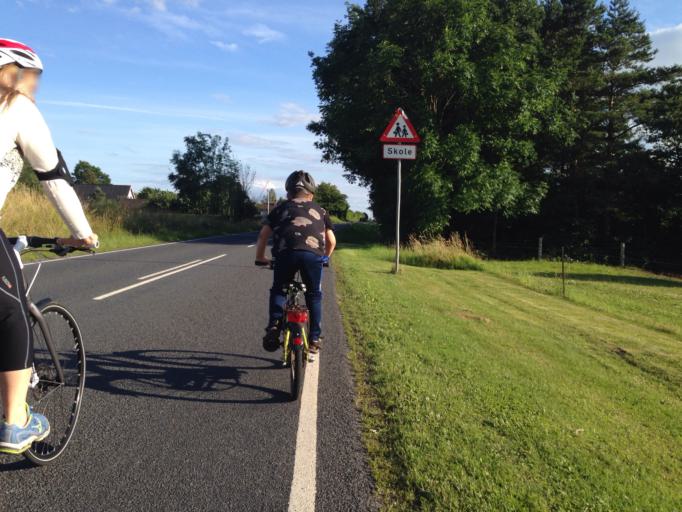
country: DK
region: South Denmark
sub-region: Middelfart Kommune
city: Norre Aby
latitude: 55.4830
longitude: 9.9020
